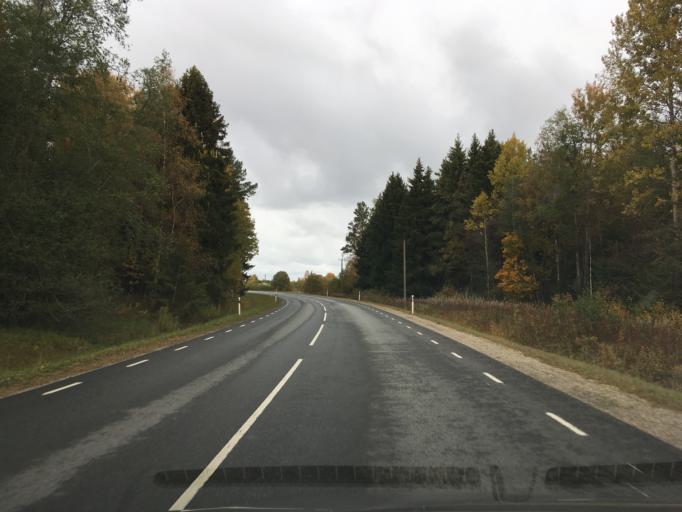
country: EE
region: Harju
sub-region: Anija vald
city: Kehra
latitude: 59.3183
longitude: 25.3437
